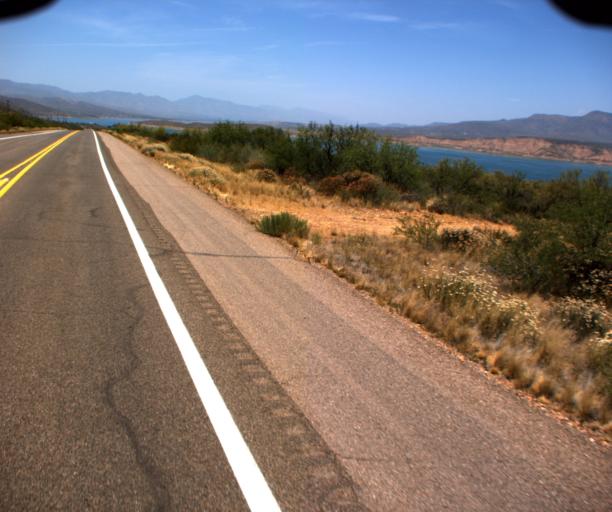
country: US
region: Arizona
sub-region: Gila County
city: Tonto Basin
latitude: 33.6548
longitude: -111.1063
